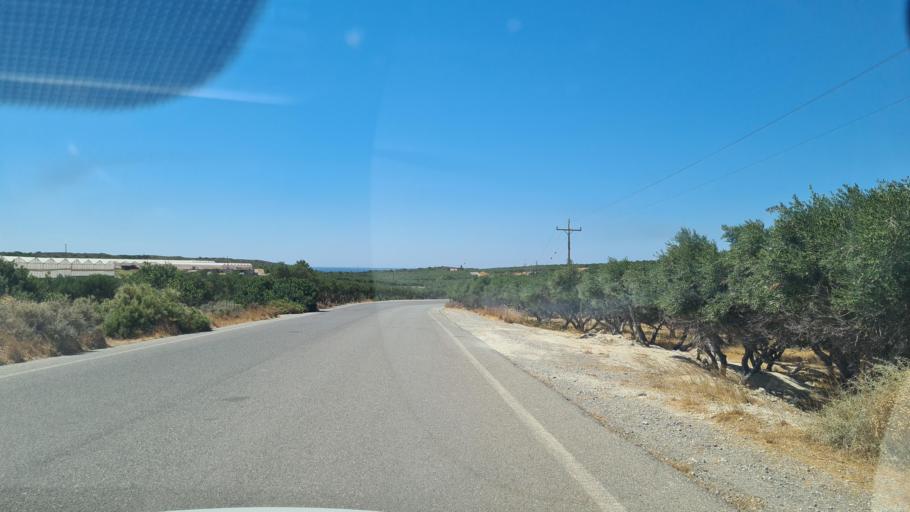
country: GR
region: Crete
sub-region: Nomos Chanias
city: Palaiochora
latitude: 35.2944
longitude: 23.5429
